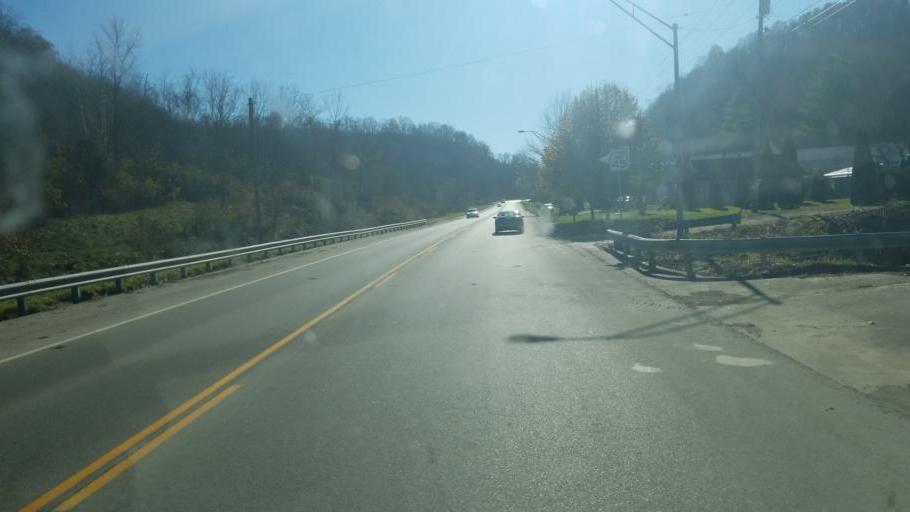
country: US
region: Kentucky
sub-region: Mason County
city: Maysville
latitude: 38.6287
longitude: -83.7504
